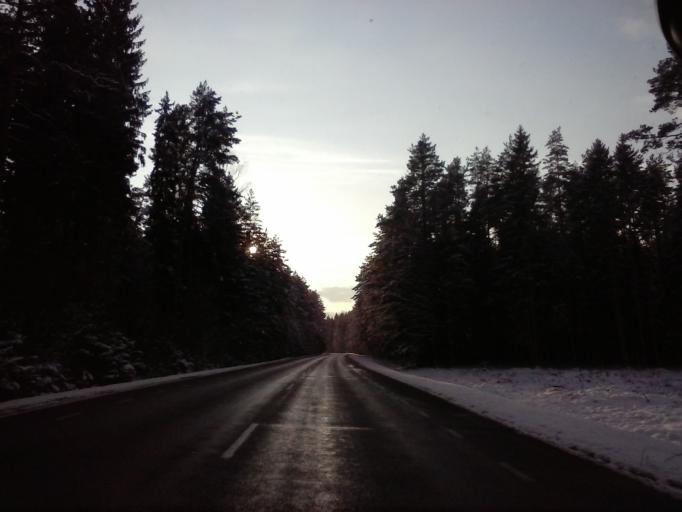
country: EE
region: Tartu
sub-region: UElenurme vald
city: Ulenurme
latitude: 58.3415
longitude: 26.9048
